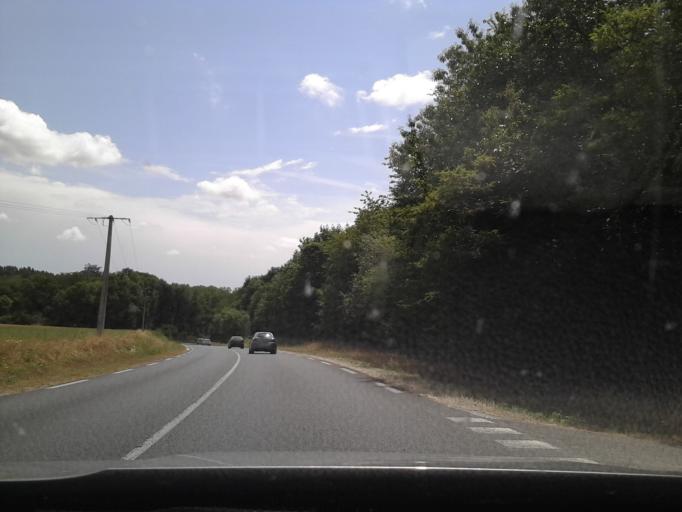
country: FR
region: Centre
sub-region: Departement d'Indre-et-Loire
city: Poce-sur-Cisse
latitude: 47.5030
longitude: 1.0000
